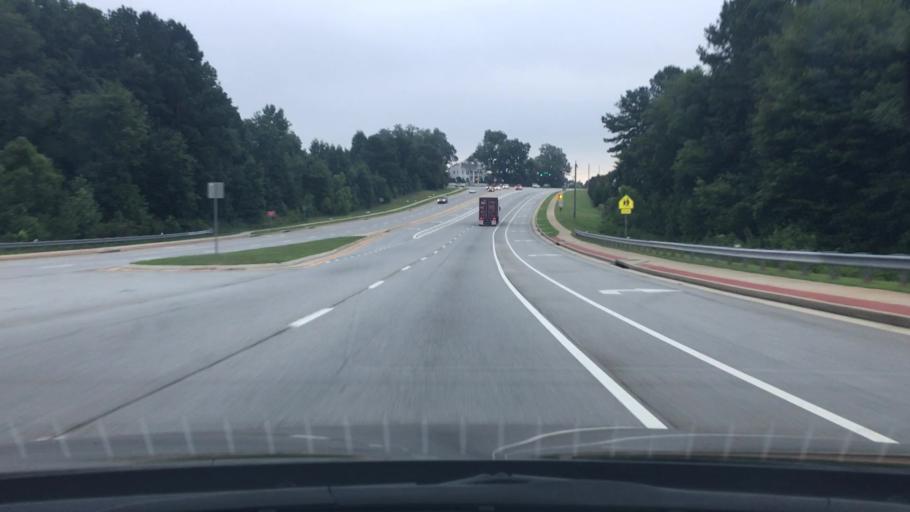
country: US
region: Georgia
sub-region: Coweta County
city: Senoia
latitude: 33.3422
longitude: -84.5293
